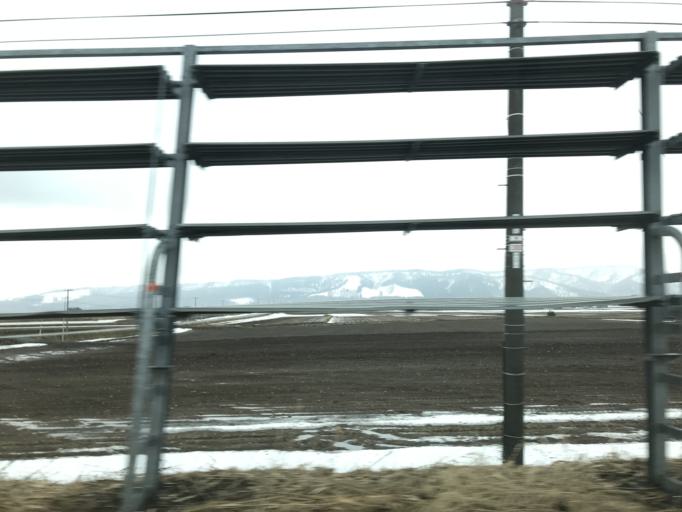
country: JP
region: Hokkaido
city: Nayoro
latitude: 44.2263
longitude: 142.3948
